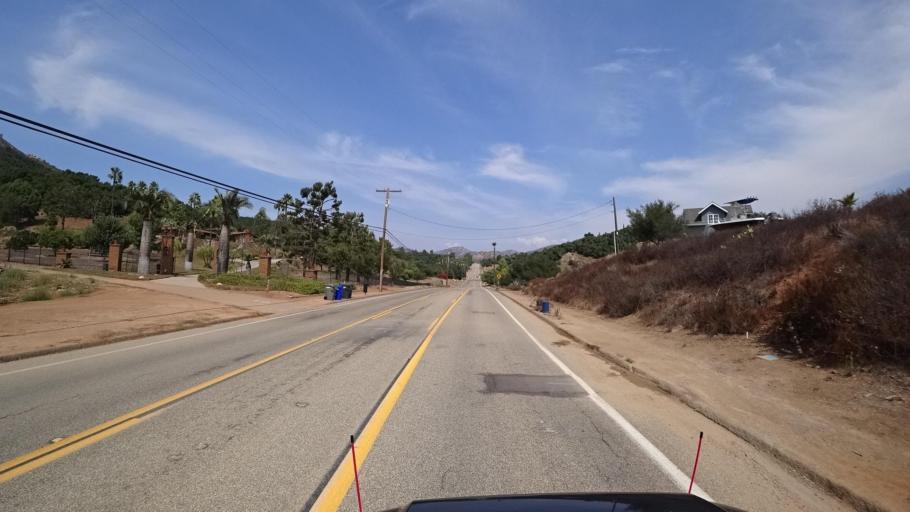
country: US
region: California
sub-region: San Diego County
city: San Pasqual
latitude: 33.1118
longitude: -117.0182
